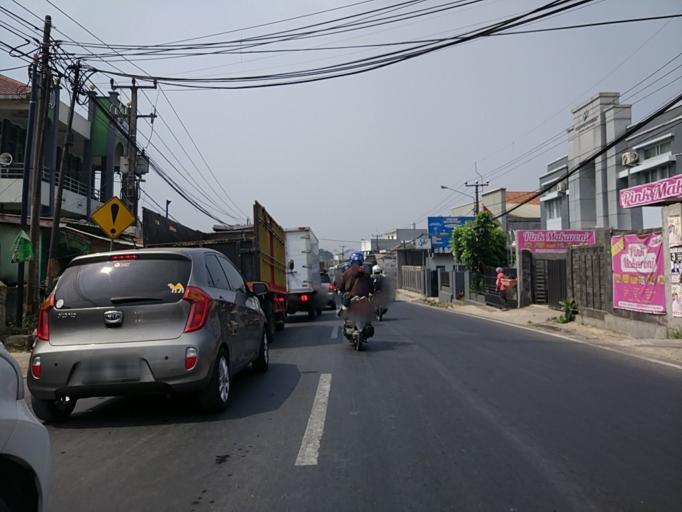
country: ID
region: West Java
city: Padalarang
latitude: -6.8375
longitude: 107.4736
